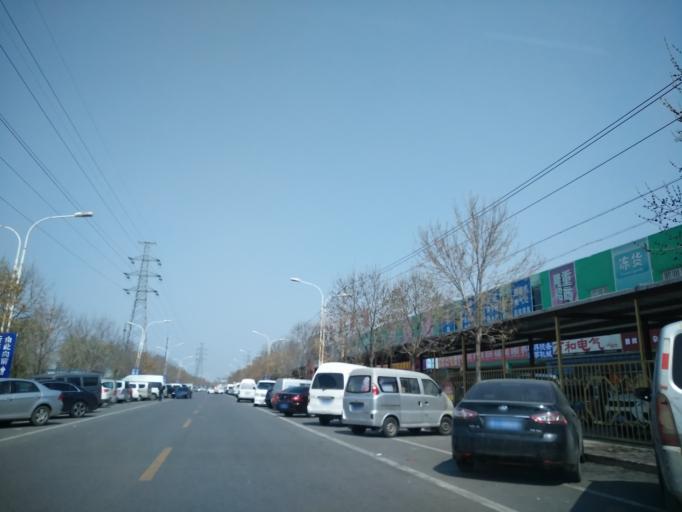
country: CN
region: Beijing
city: Qingyundian
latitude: 39.7553
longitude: 116.5334
